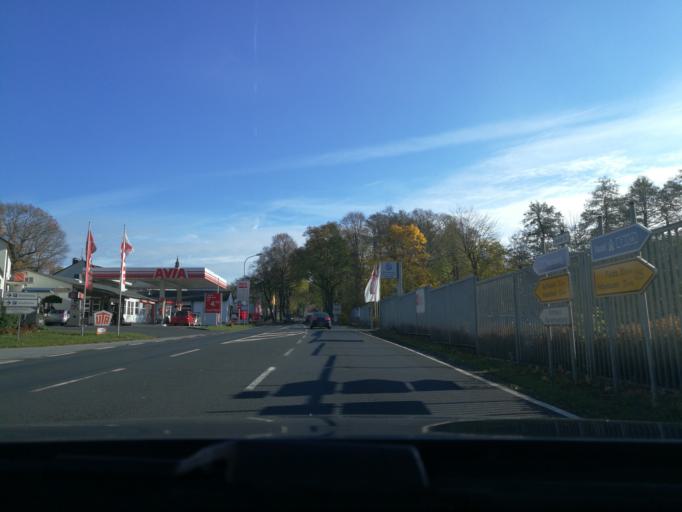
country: DE
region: Hesse
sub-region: Regierungsbezirk Kassel
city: Gersfeld
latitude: 50.4515
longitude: 9.9118
